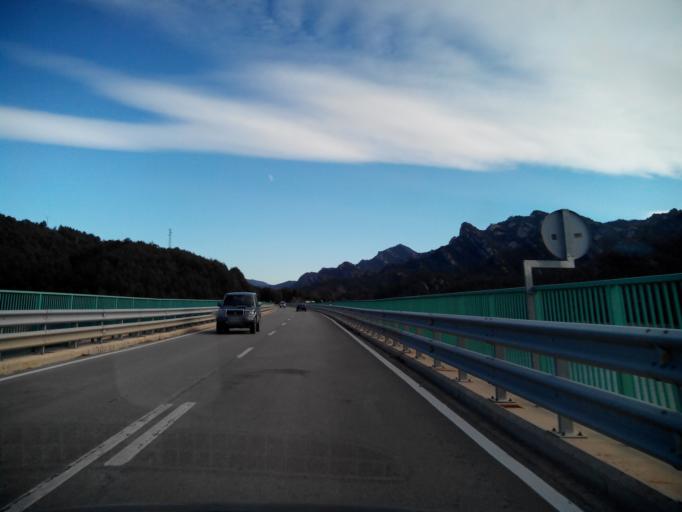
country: ES
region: Catalonia
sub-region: Provincia de Barcelona
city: Berga
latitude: 42.1269
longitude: 1.8795
